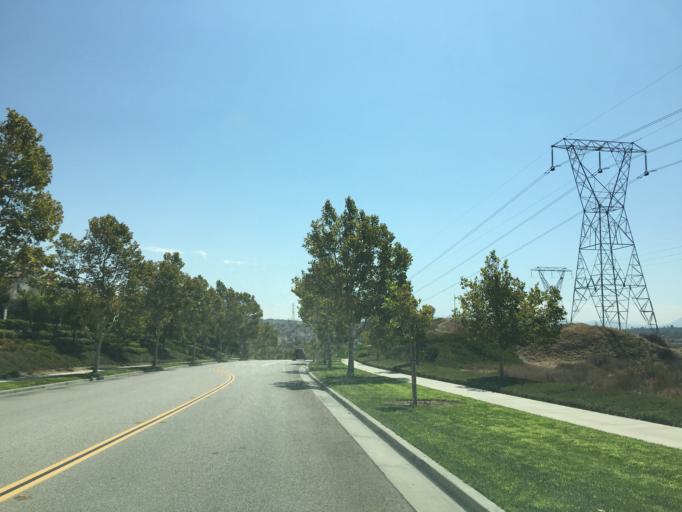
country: US
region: California
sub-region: Los Angeles County
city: Valencia
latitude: 34.4674
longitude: -118.5609
